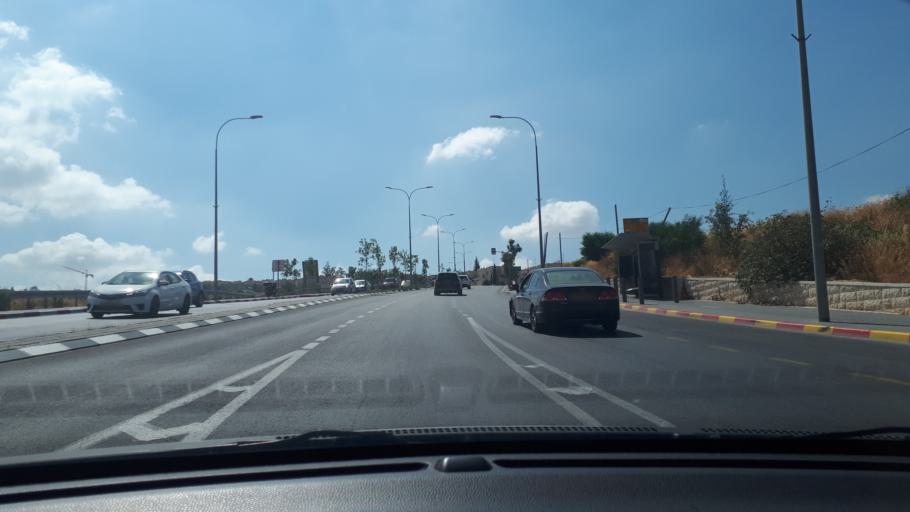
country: PS
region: West Bank
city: Hizma
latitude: 31.8279
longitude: 35.2512
